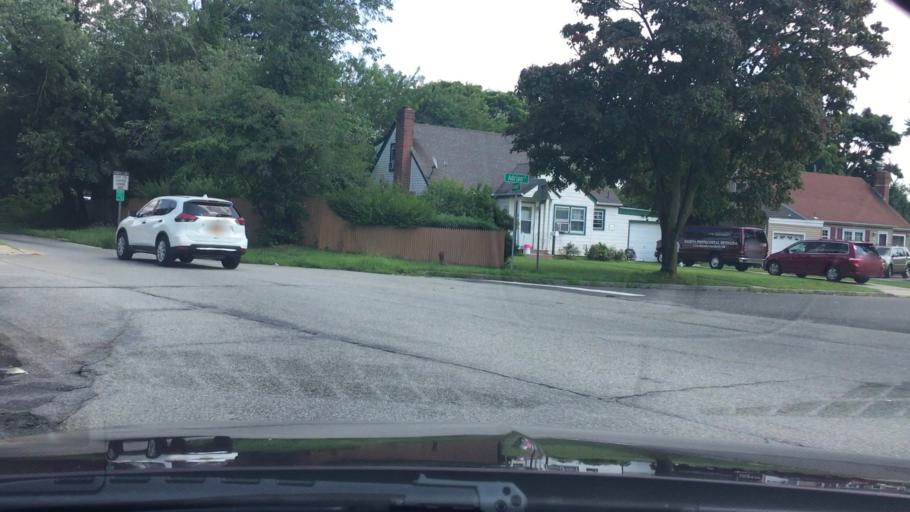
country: US
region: New York
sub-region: Suffolk County
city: North Amityville
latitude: 40.7056
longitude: -73.4289
